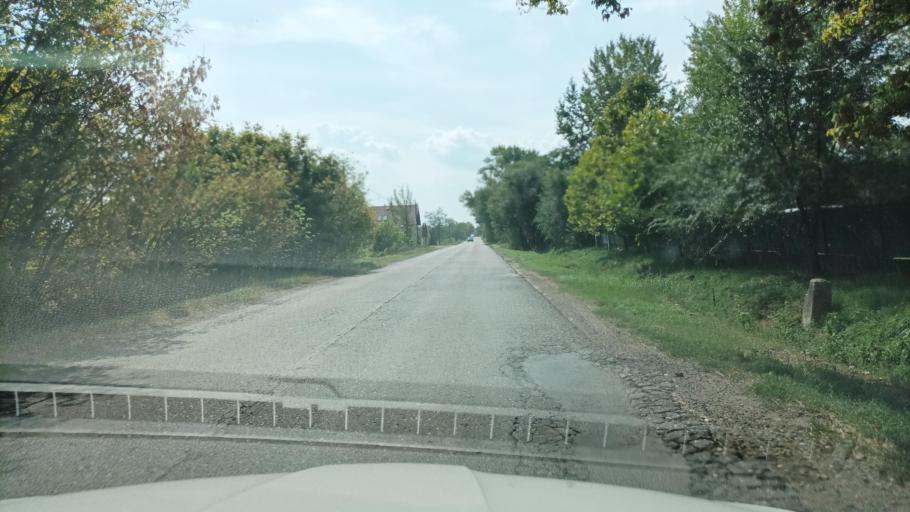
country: HU
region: Pest
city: Tura
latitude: 47.6170
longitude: 19.6095
